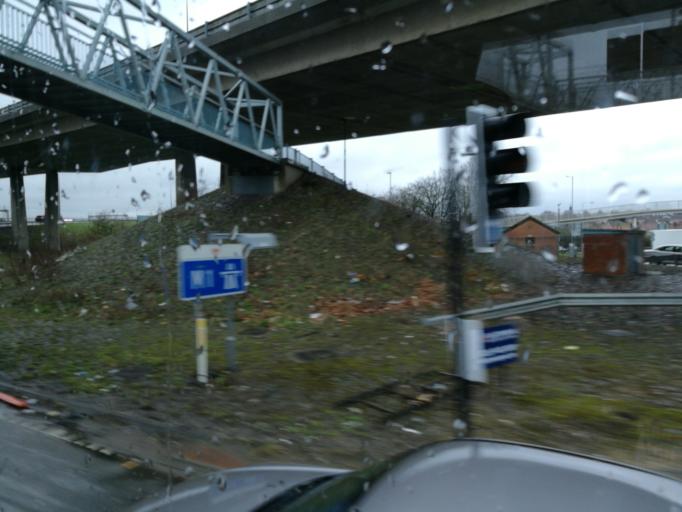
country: GB
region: England
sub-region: Greater London
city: Hendon
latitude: 51.5724
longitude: -0.2274
